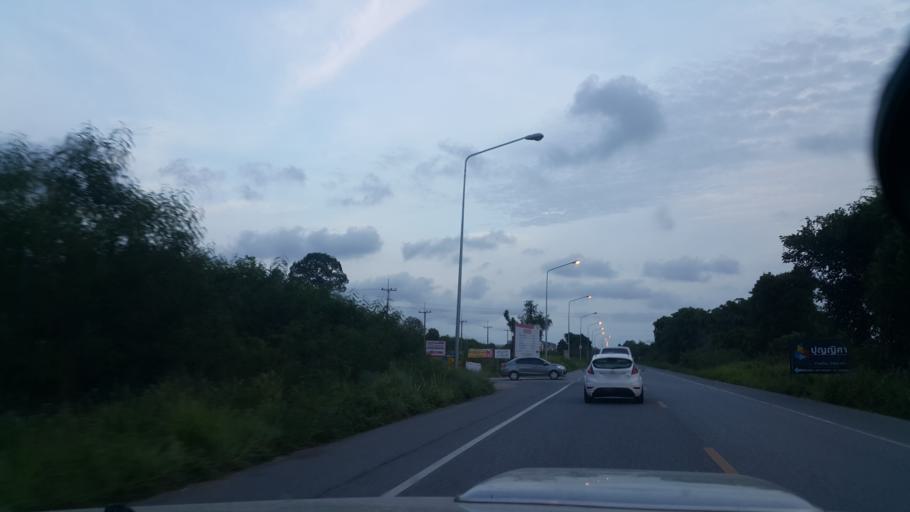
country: TH
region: Rayong
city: Ban Chang
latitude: 12.7171
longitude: 100.9958
